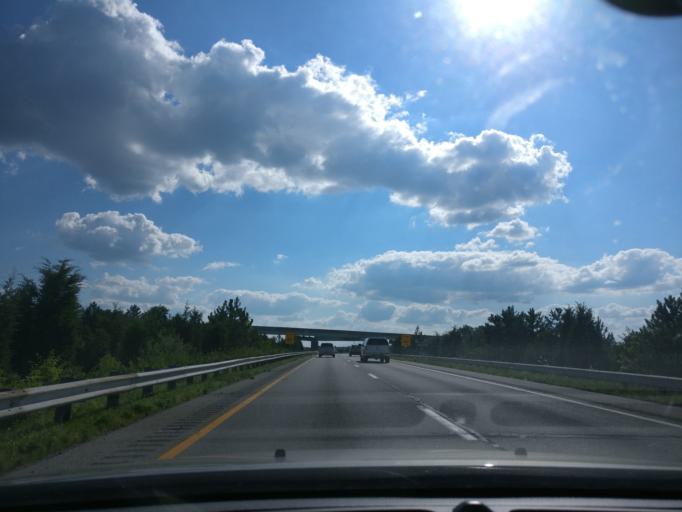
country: US
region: Ohio
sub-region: Montgomery County
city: West Carrollton City
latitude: 39.6237
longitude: -84.2278
